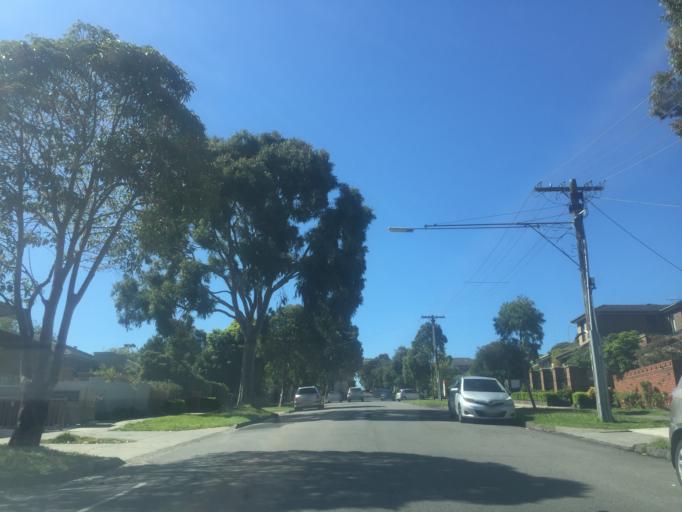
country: AU
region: Victoria
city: Mont Albert
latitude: -37.8135
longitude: 145.0907
